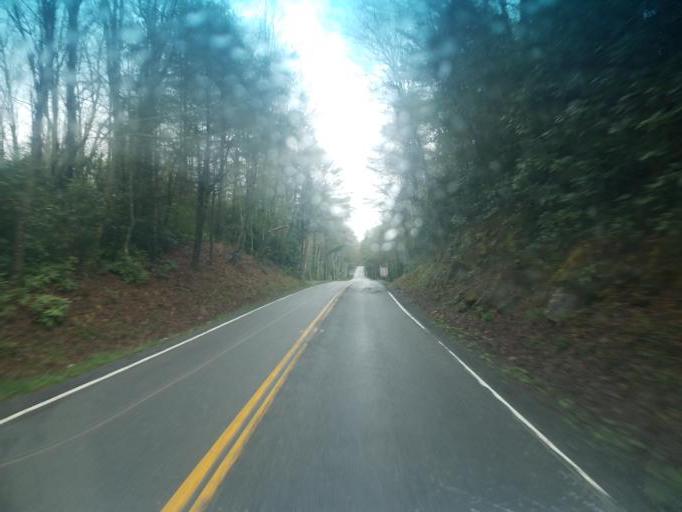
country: US
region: Virginia
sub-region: Smyth County
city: Chilhowie
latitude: 36.6533
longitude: -81.6972
